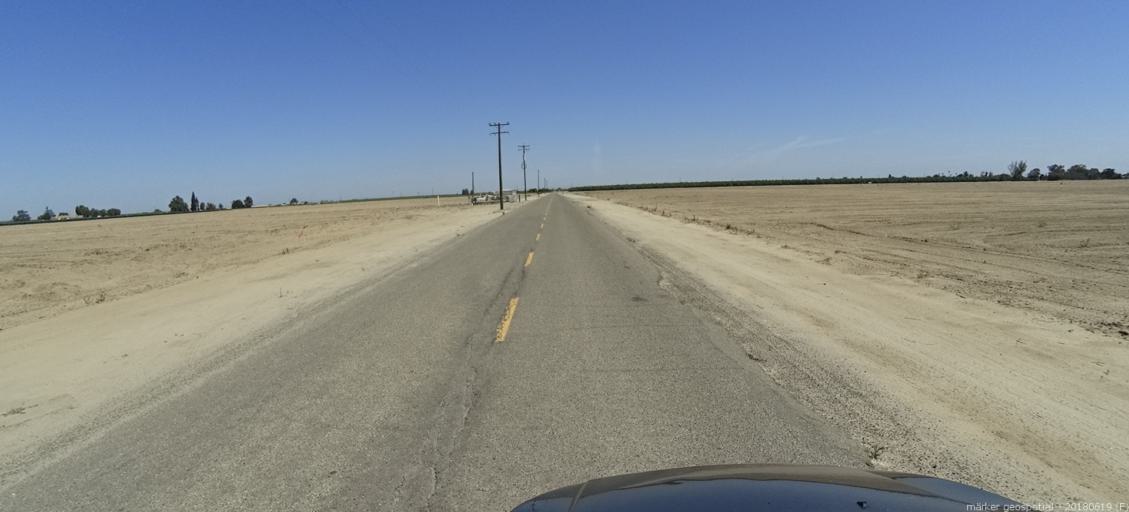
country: US
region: California
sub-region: Fresno County
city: Biola
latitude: 36.8449
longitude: -120.0649
